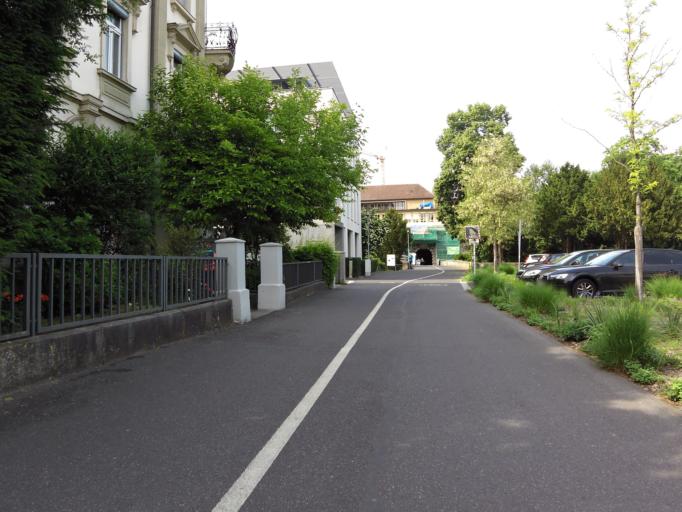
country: DE
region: Bavaria
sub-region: Regierungsbezirk Unterfranken
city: Wuerzburg
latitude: 49.7880
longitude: 9.9245
